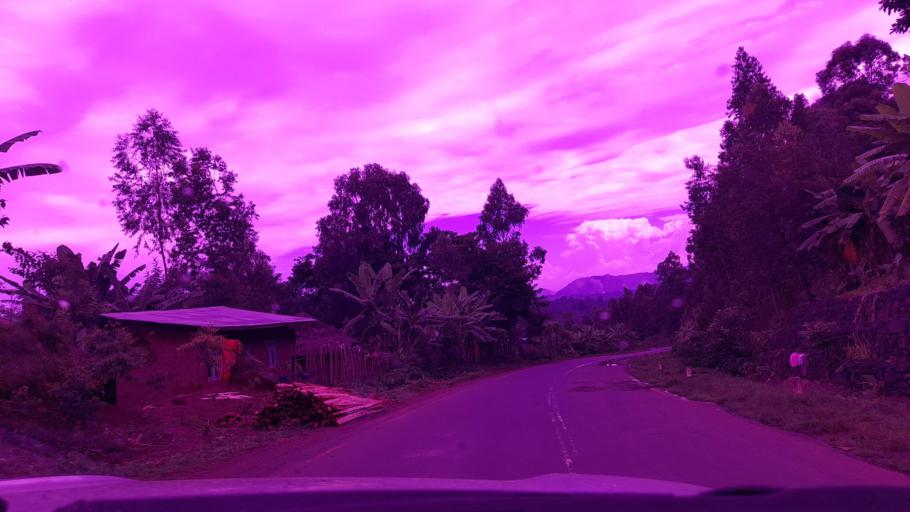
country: ET
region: Southern Nations, Nationalities, and People's Region
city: Mizan Teferi
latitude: 7.0635
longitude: 35.6302
